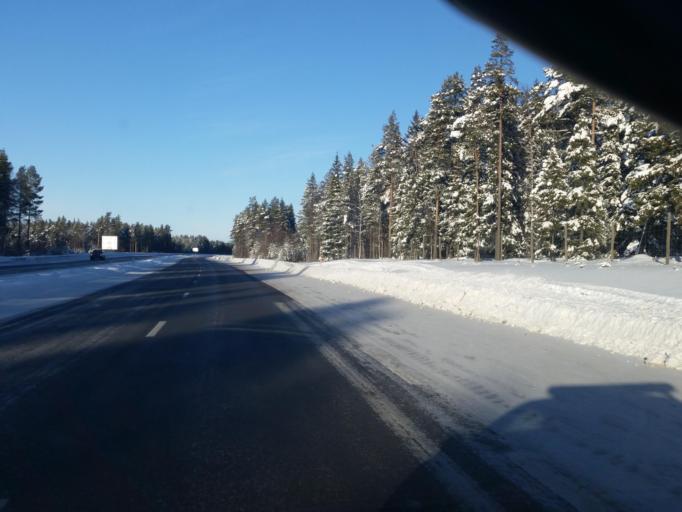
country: SE
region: Norrbotten
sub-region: Pitea Kommun
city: Pitea
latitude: 65.3375
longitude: 21.4409
